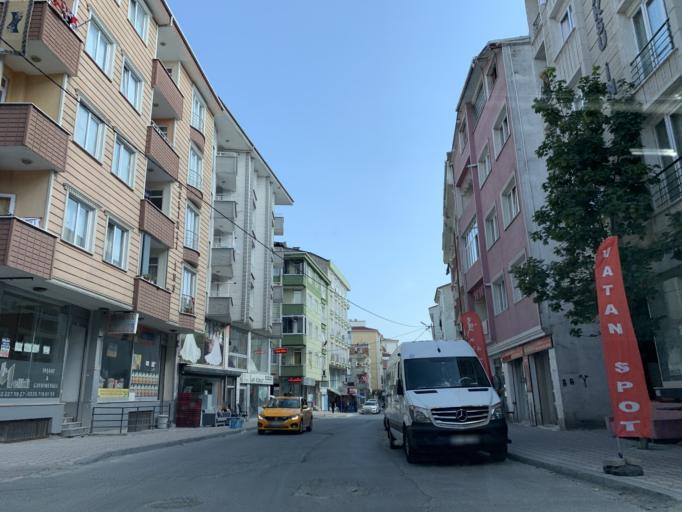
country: TR
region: Istanbul
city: Esenyurt
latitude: 41.0369
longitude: 28.6753
